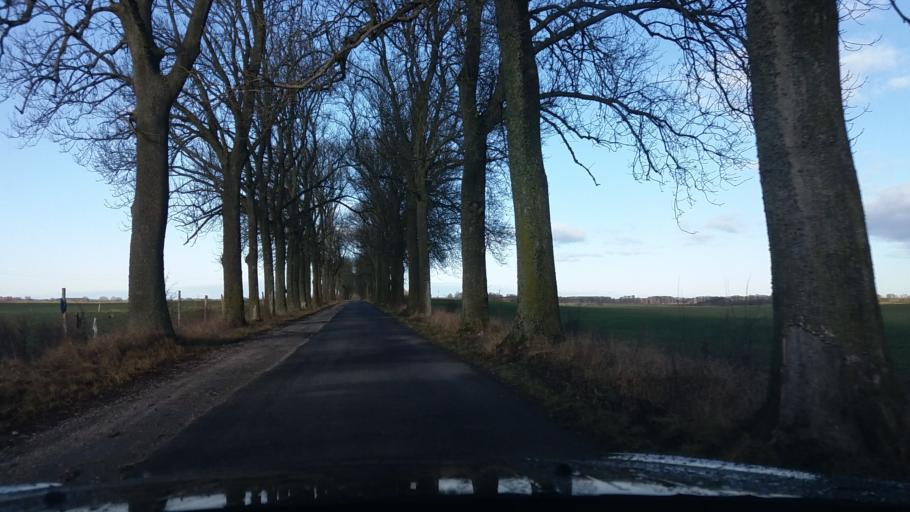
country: PL
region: West Pomeranian Voivodeship
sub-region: Powiat choszczenski
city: Drawno
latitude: 53.1959
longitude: 15.7858
